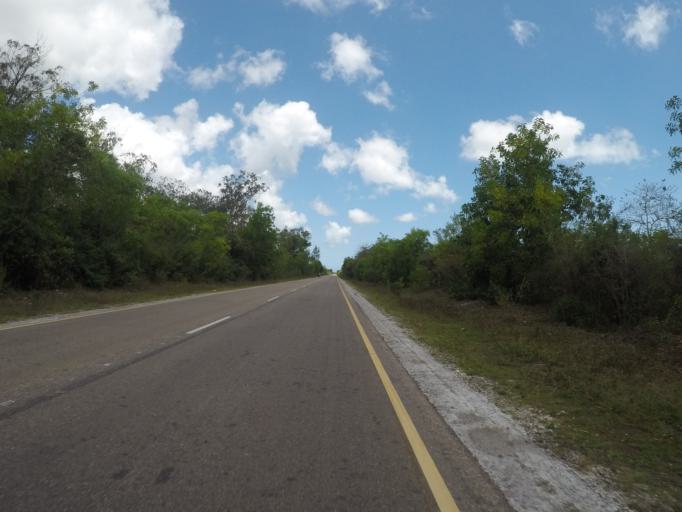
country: TZ
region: Zanzibar Central/South
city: Koani
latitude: -6.2586
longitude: 39.3582
